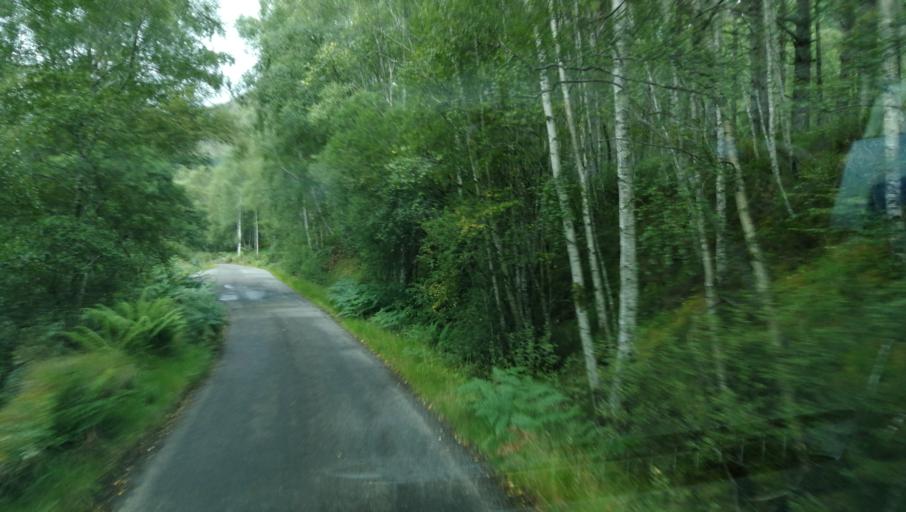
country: GB
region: Scotland
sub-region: Highland
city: Spean Bridge
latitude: 57.3125
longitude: -4.8544
